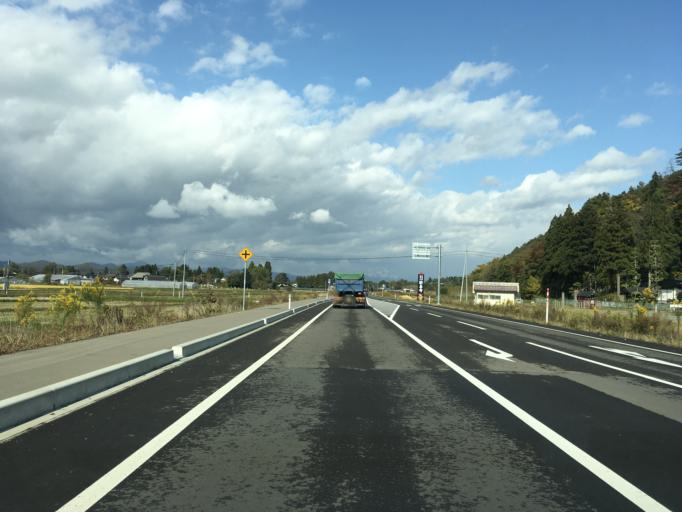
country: JP
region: Iwate
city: Hanamaki
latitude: 39.3670
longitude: 141.1491
